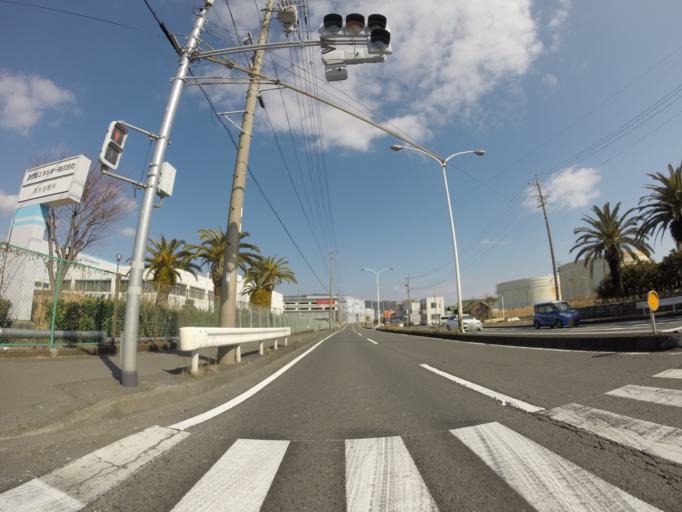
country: JP
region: Shizuoka
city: Shizuoka-shi
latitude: 35.0298
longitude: 138.4926
